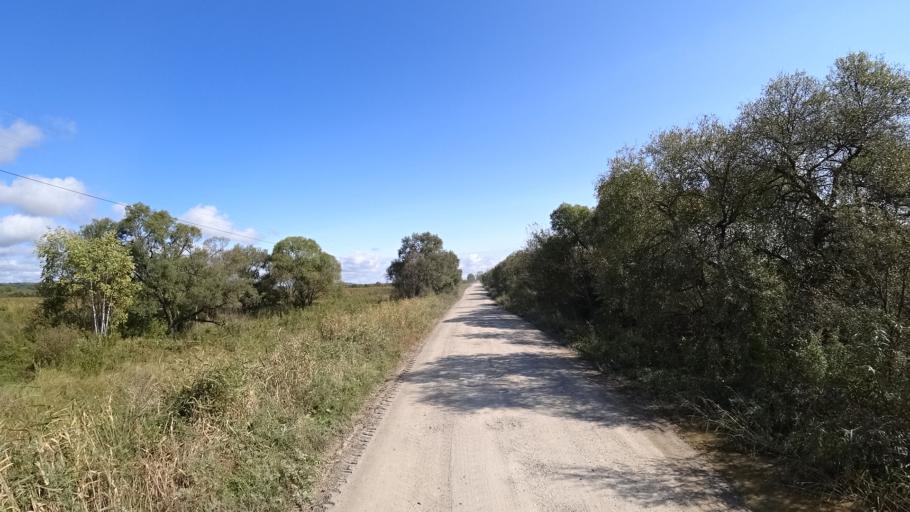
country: RU
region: Amur
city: Arkhara
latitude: 49.4105
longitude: 130.1640
